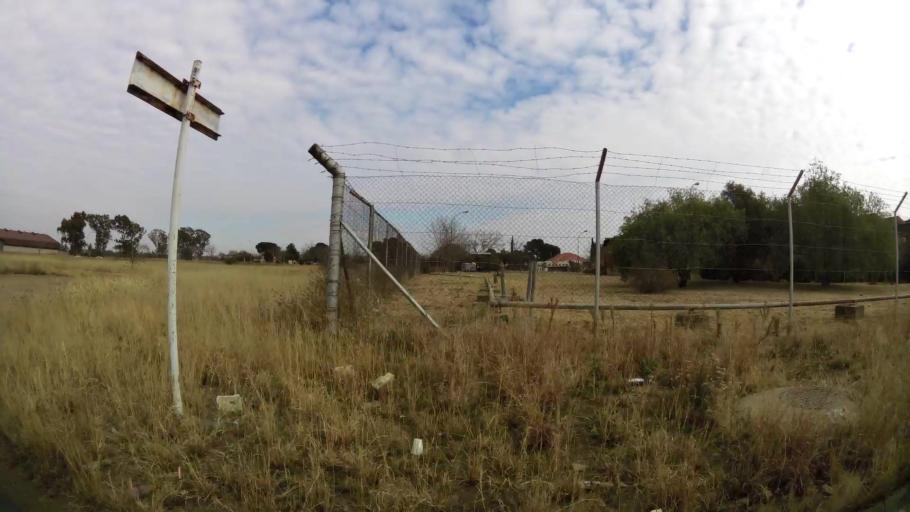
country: ZA
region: Orange Free State
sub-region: Mangaung Metropolitan Municipality
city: Bloemfontein
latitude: -29.1320
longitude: 26.2042
